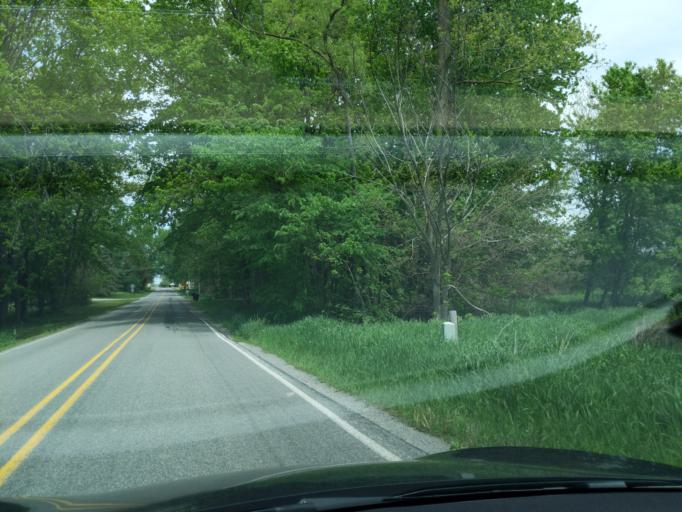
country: US
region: Michigan
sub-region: Ingham County
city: Stockbridge
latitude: 42.4651
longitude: -84.1610
